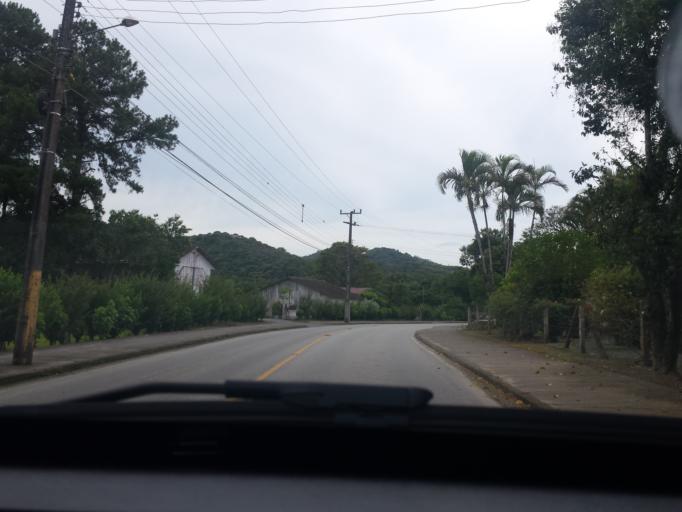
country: BR
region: Santa Catarina
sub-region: Gaspar
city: Gaspar
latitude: -26.8917
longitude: -49.0083
